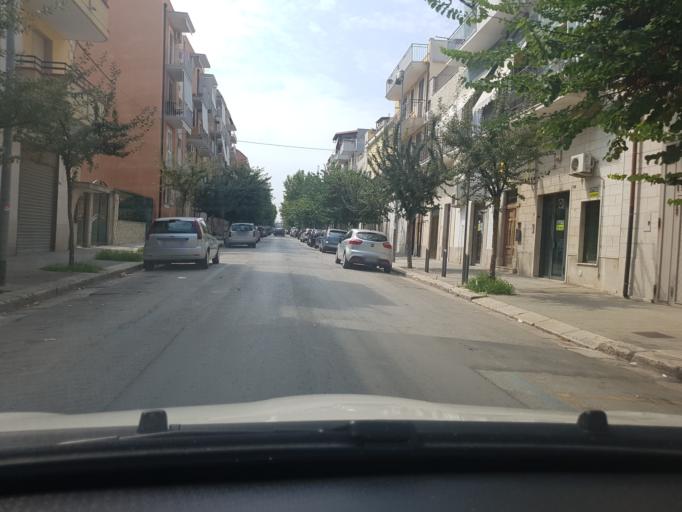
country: IT
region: Apulia
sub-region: Provincia di Foggia
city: Cerignola
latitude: 41.2672
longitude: 15.9037
